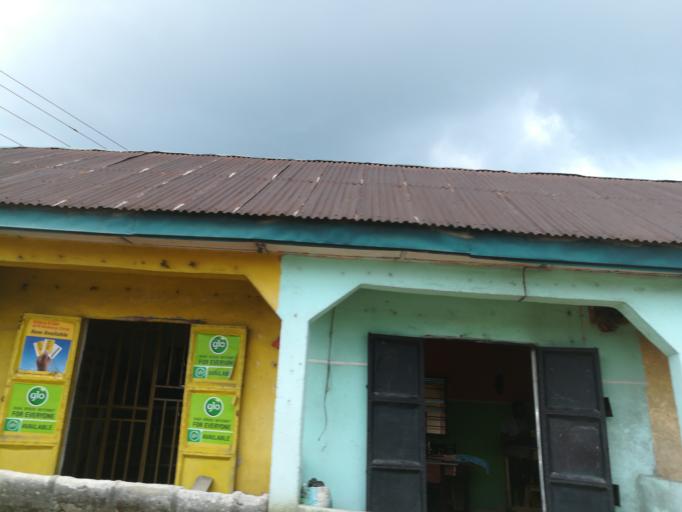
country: NG
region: Rivers
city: Okrika
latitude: 4.7261
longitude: 7.1522
